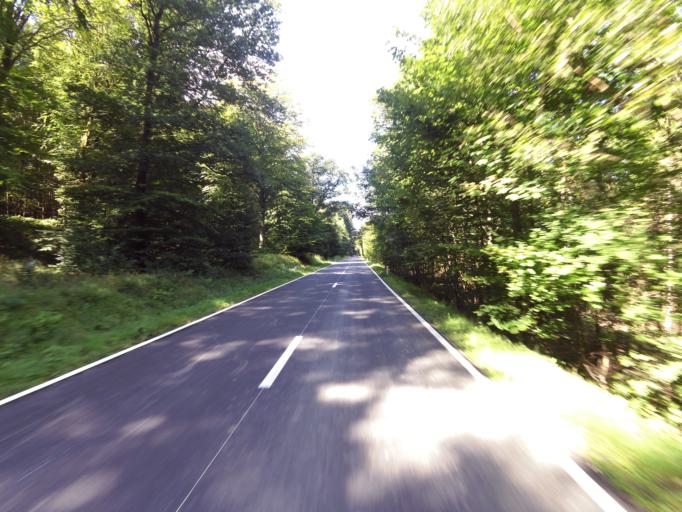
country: BE
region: Wallonia
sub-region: Province du Luxembourg
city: Nassogne
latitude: 50.1273
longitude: 5.3750
